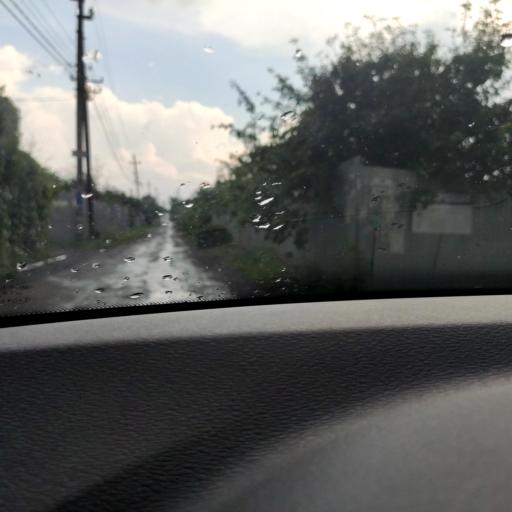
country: RU
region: Samara
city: Novosemeykino
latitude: 53.4016
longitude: 50.3147
